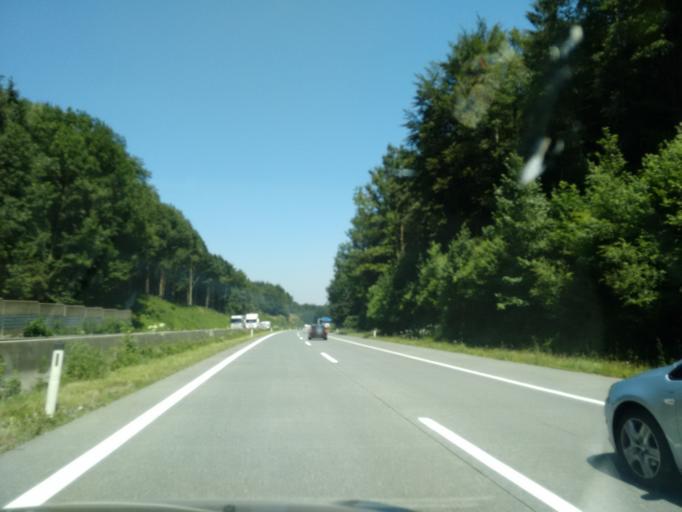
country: AT
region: Upper Austria
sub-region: Politischer Bezirk Vocklabruck
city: Desselbrunn
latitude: 47.9890
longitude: 13.7803
